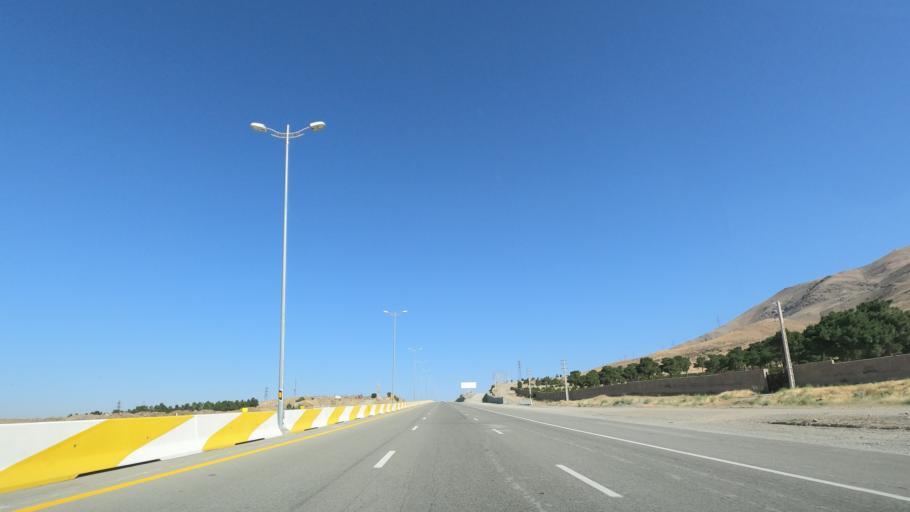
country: IR
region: Tehran
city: Shahr-e Qods
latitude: 35.7637
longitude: 51.0712
